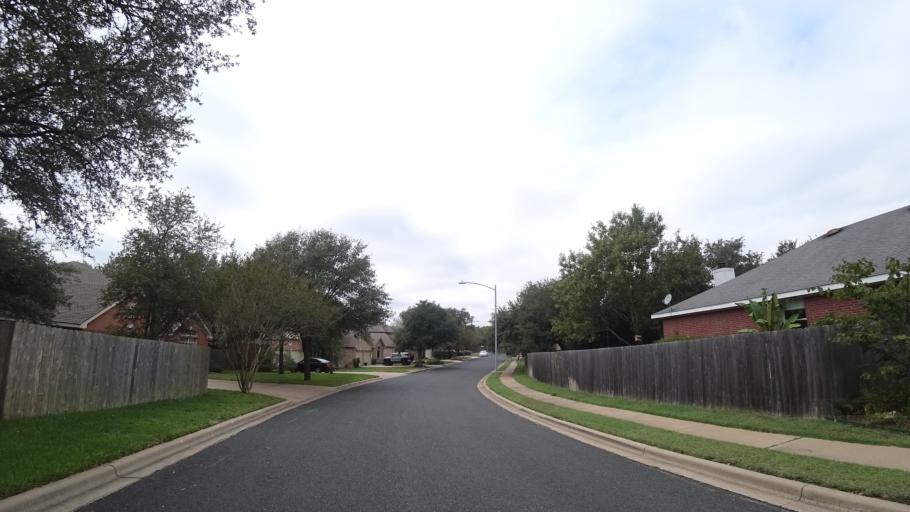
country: US
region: Texas
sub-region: Travis County
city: Shady Hollow
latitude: 30.2186
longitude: -97.8756
